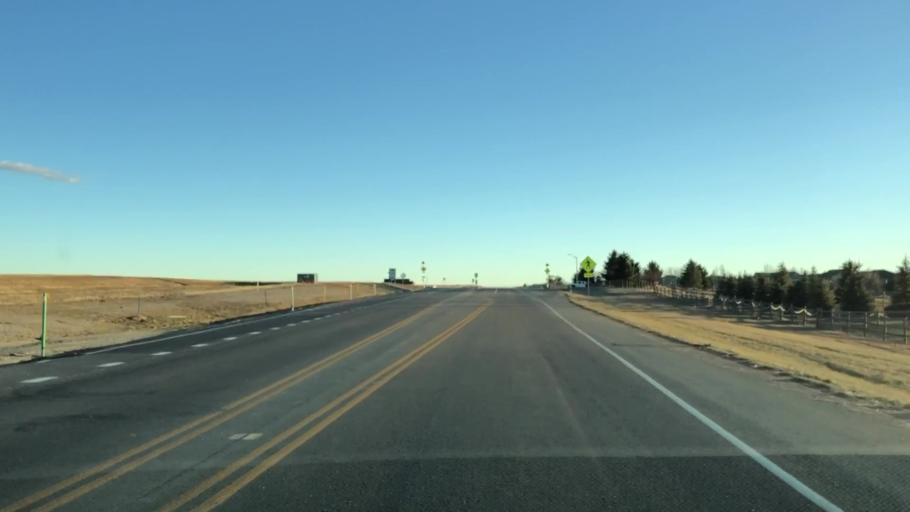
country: US
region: Colorado
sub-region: Weld County
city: Windsor
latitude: 40.4475
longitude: -104.9441
